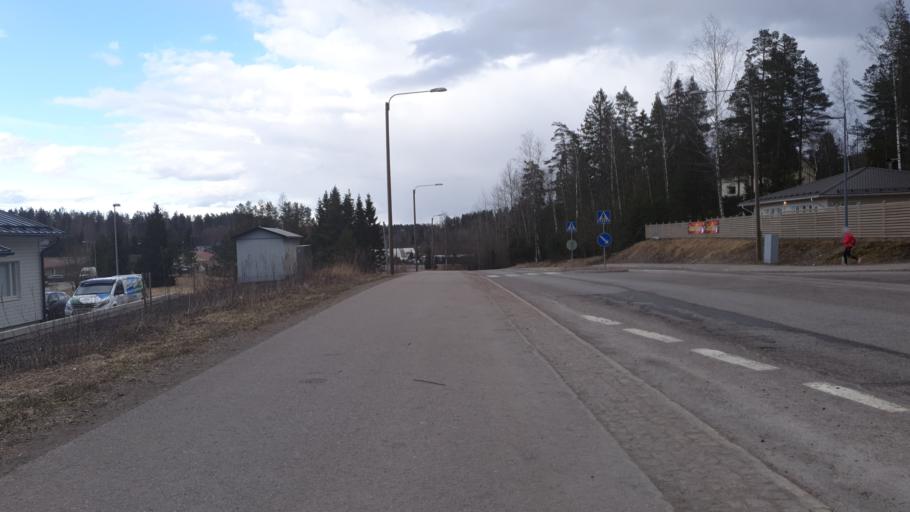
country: FI
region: Uusimaa
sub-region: Helsinki
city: Nurmijaervi
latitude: 60.3647
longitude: 24.7491
